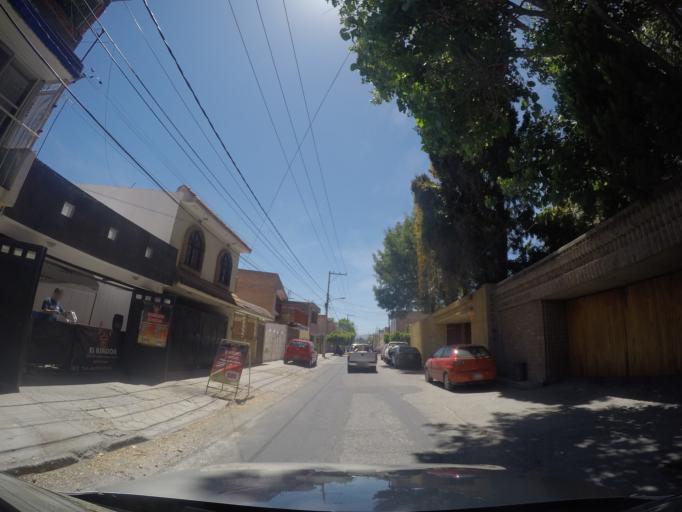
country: MX
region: San Luis Potosi
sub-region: San Luis Potosi
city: San Luis Potosi
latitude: 22.1588
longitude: -100.9934
